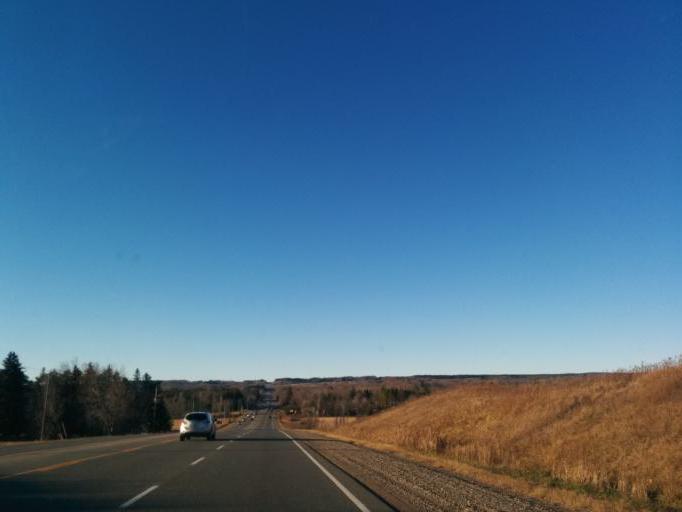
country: CA
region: Ontario
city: Orangeville
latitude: 43.8169
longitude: -79.9370
